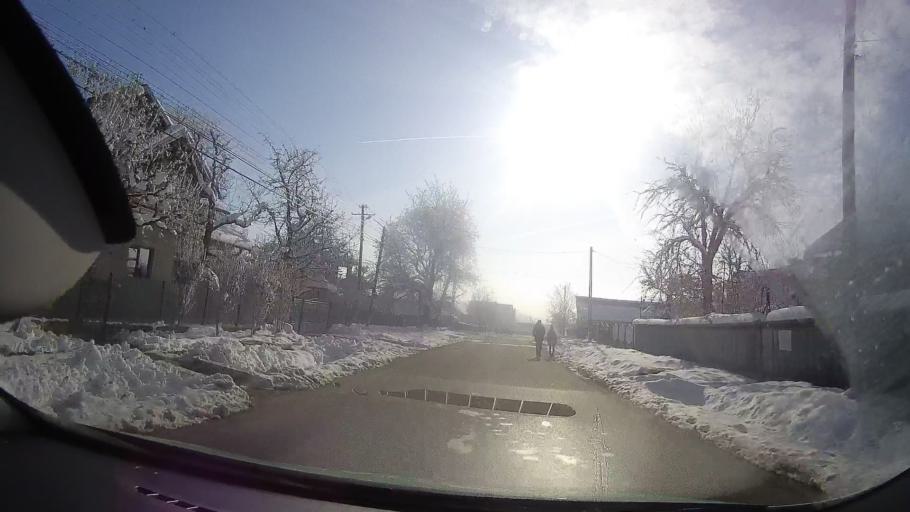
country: RO
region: Iasi
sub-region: Comuna Cristesti
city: Cristesti
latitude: 47.2583
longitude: 26.5750
